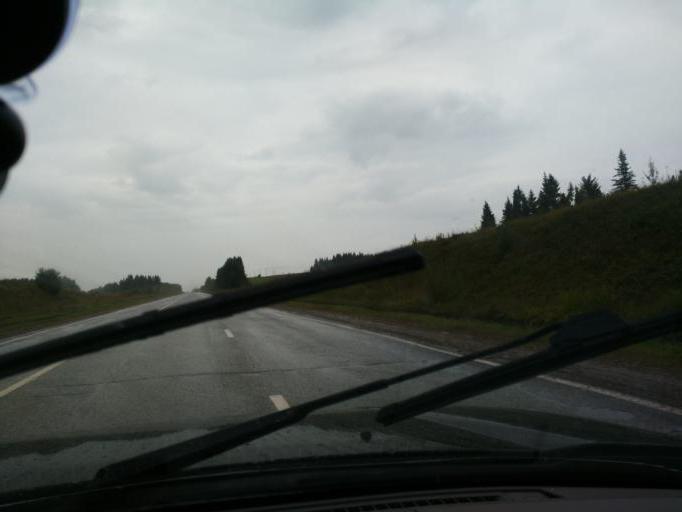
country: RU
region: Perm
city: Yugo-Kamskiy
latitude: 57.4877
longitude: 55.6833
